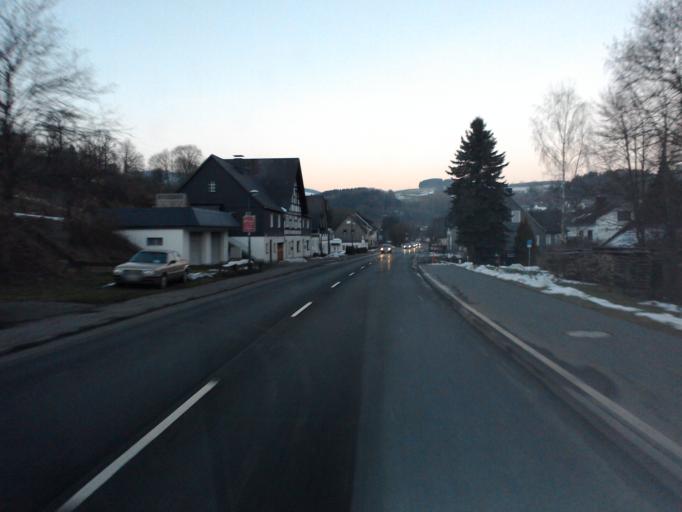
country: DE
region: North Rhine-Westphalia
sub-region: Regierungsbezirk Arnsberg
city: Olsberg
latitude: 51.3044
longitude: 8.4995
